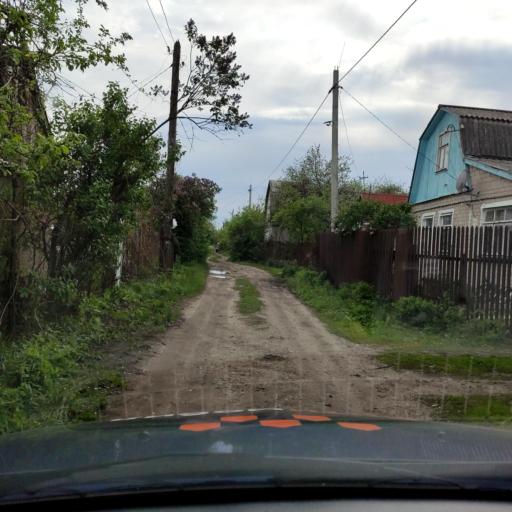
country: RU
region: Voronezj
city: Voronezh
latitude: 51.5973
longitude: 39.1539
